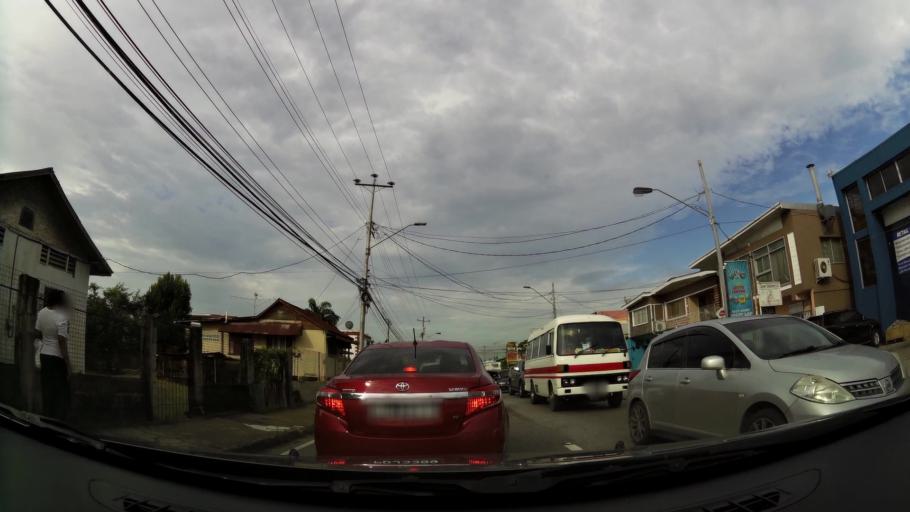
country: TT
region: San Juan/Laventille
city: Laventille
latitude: 10.6510
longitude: -61.4426
